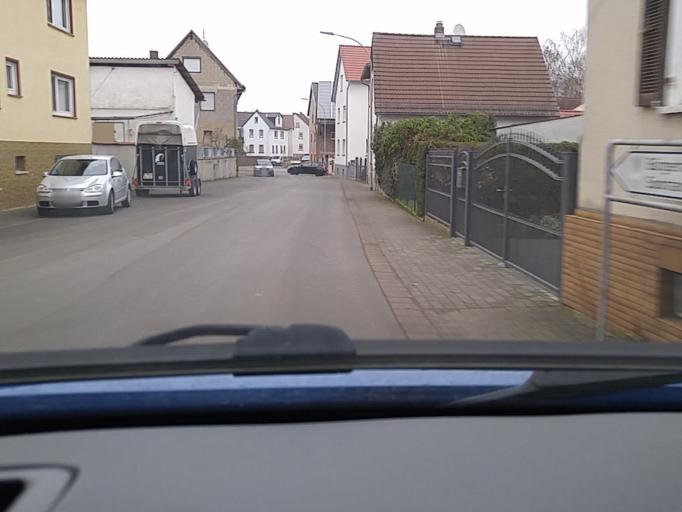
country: DE
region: Hesse
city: Reichelsheim
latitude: 50.3554
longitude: 8.8750
